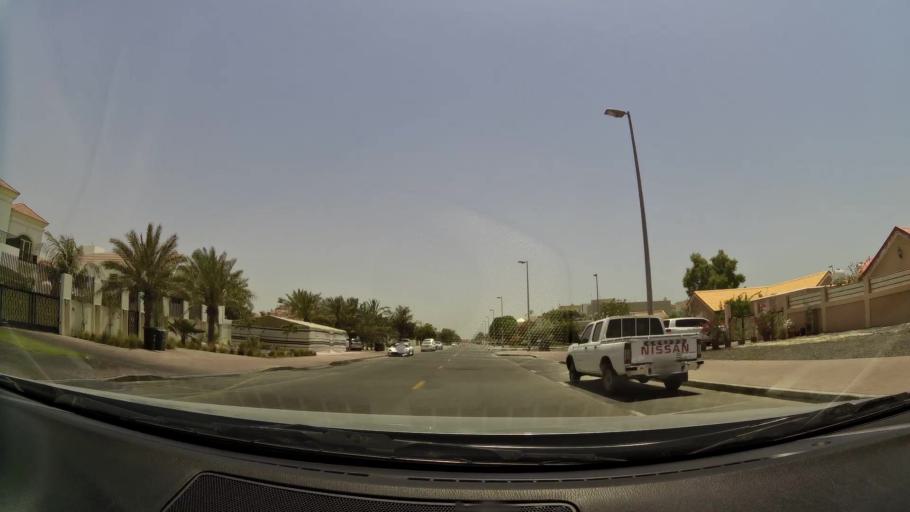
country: AE
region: Dubai
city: Dubai
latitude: 25.2060
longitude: 55.2468
